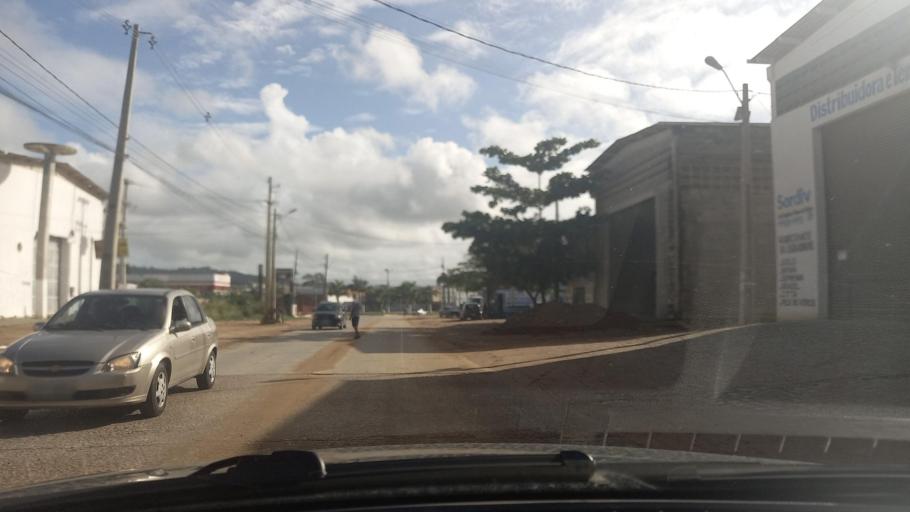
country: BR
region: Pernambuco
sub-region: Vitoria De Santo Antao
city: Vitoria de Santo Antao
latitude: -8.1162
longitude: -35.2818
